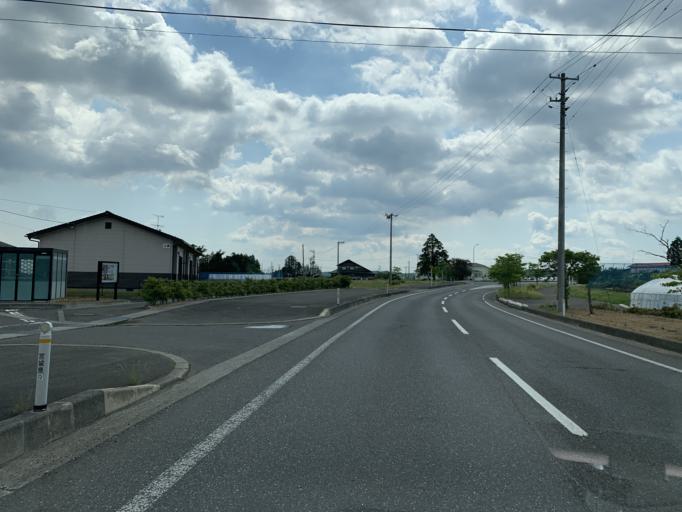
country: JP
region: Miyagi
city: Furukawa
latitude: 38.7420
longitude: 140.9581
